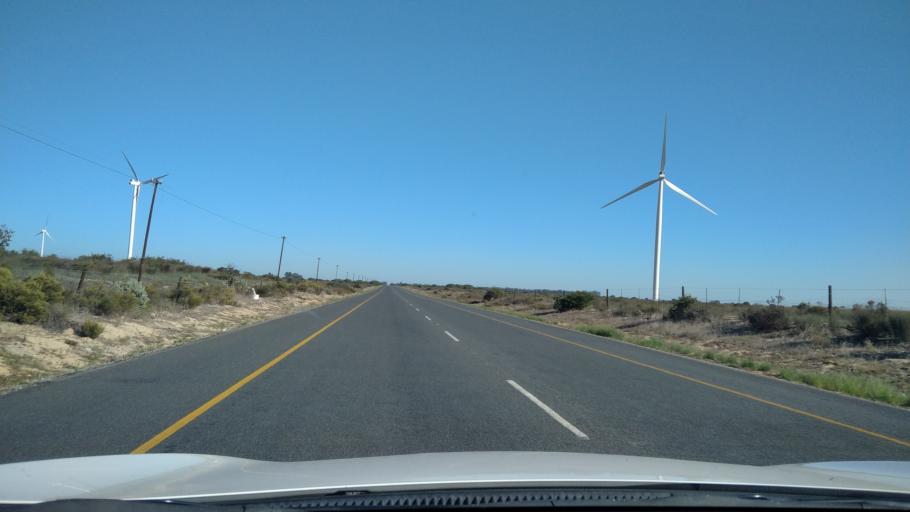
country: ZA
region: Western Cape
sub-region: West Coast District Municipality
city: Moorreesburg
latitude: -33.0871
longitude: 18.4004
